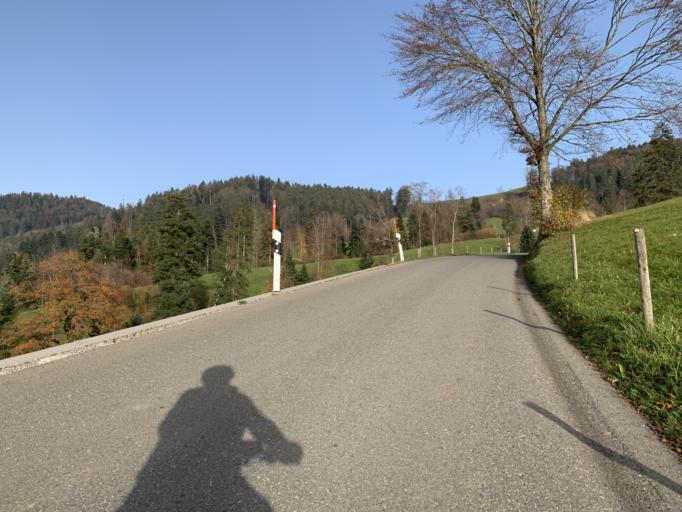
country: CH
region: Zurich
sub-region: Bezirk Hinwil
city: Hadlikon
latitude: 47.3034
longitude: 8.8788
